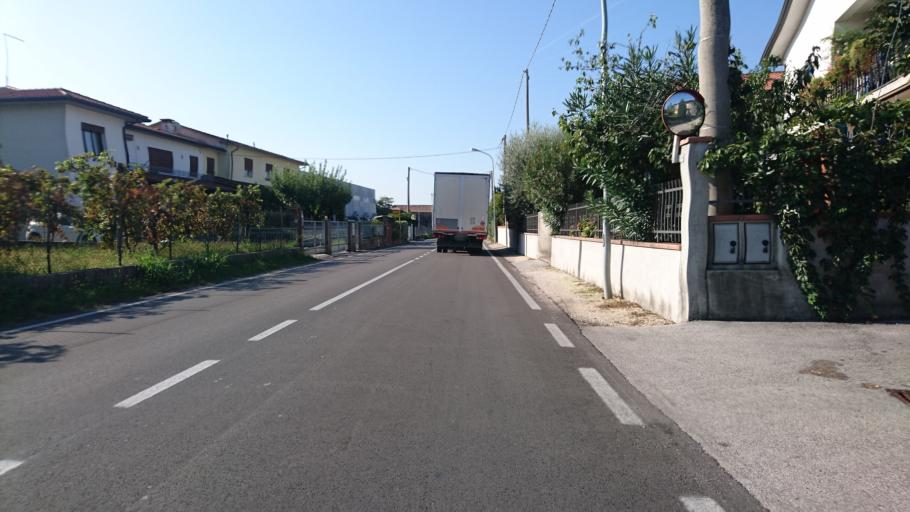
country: IT
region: Veneto
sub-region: Provincia di Vicenza
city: Bassano del Grappa
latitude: 45.7499
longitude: 11.7240
